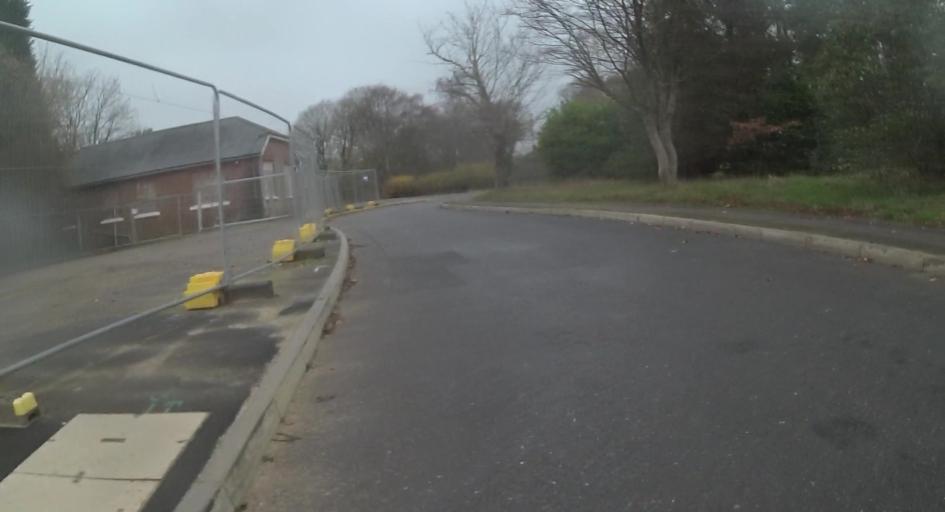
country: GB
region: England
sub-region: Surrey
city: Frimley
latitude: 51.3104
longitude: -0.6958
